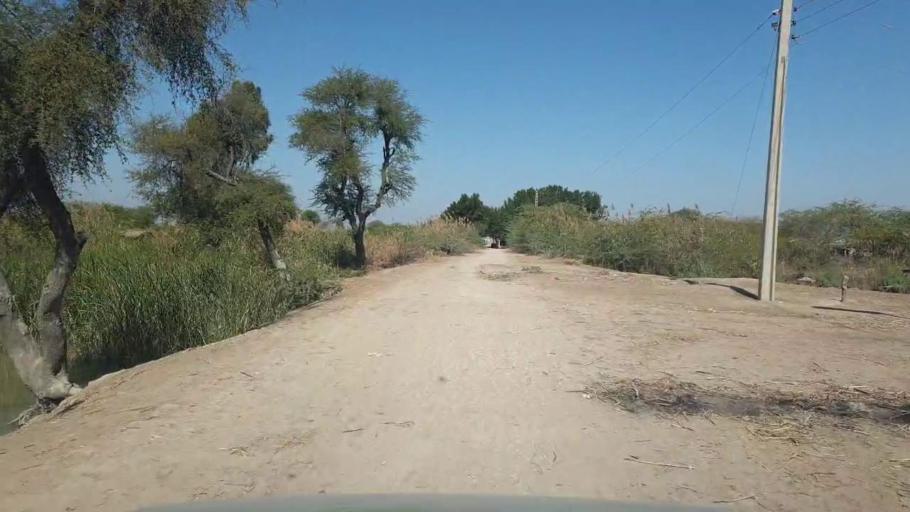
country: PK
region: Sindh
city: Mirwah Gorchani
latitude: 25.3182
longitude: 69.1278
